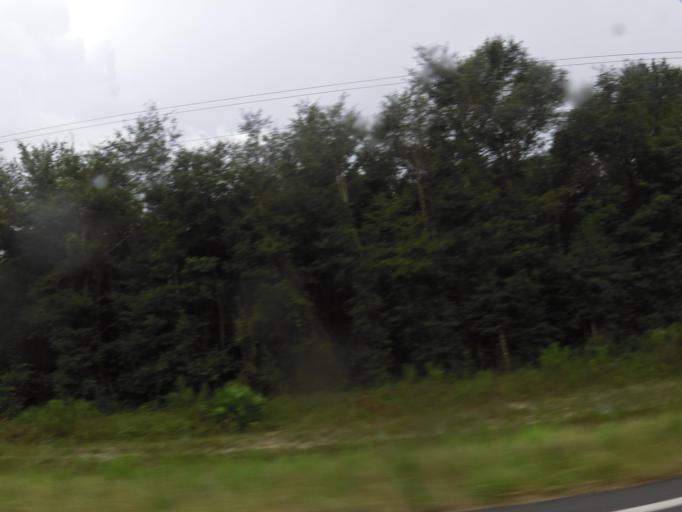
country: US
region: Florida
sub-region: Baker County
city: Macclenny
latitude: 30.3852
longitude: -82.1736
